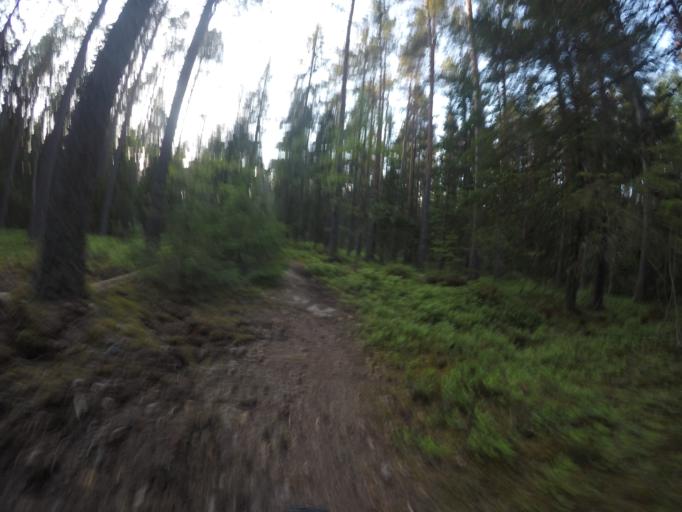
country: SE
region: Soedermanland
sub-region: Eskilstuna Kommun
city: Skogstorp
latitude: 59.3313
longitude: 16.5176
